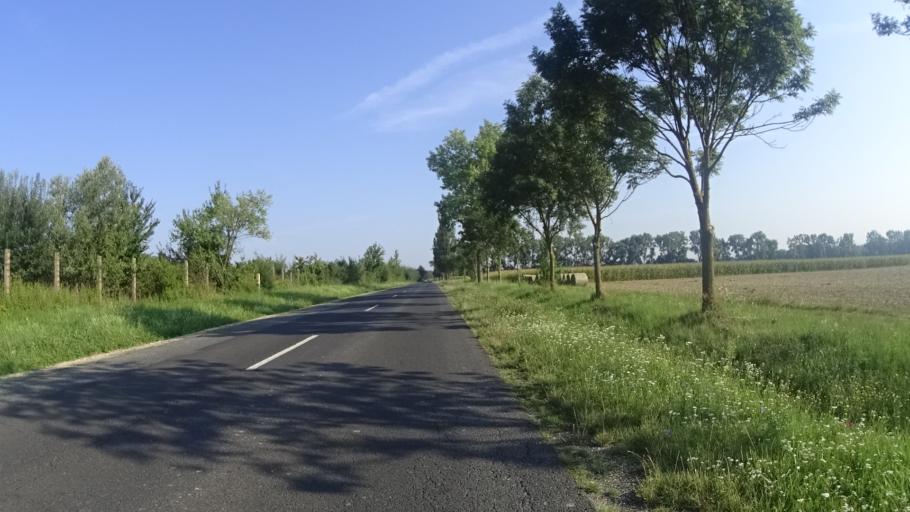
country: HU
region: Zala
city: Sarmellek
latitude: 46.6801
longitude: 17.1707
